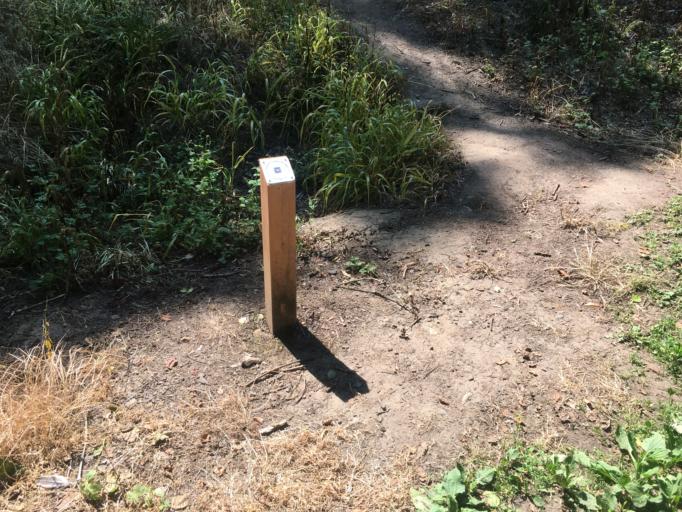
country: GB
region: England
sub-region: Surrey
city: Chilworth
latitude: 51.2172
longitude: -0.5274
